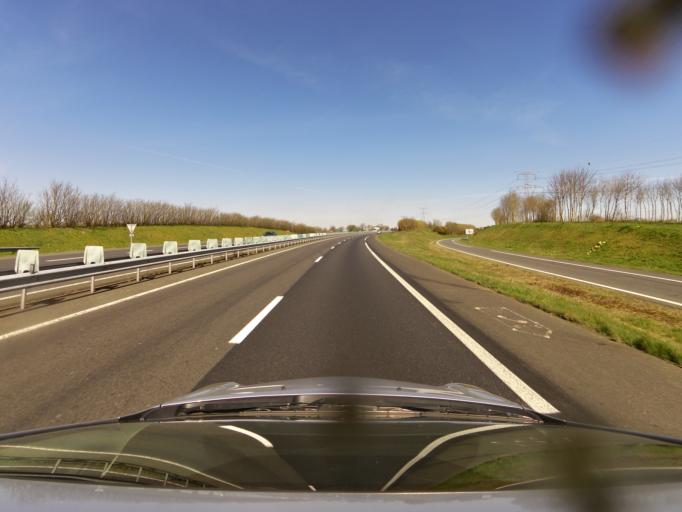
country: FR
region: Lower Normandy
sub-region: Departement de la Manche
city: Villedieu-les-Poeles
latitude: 48.8385
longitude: -1.2486
